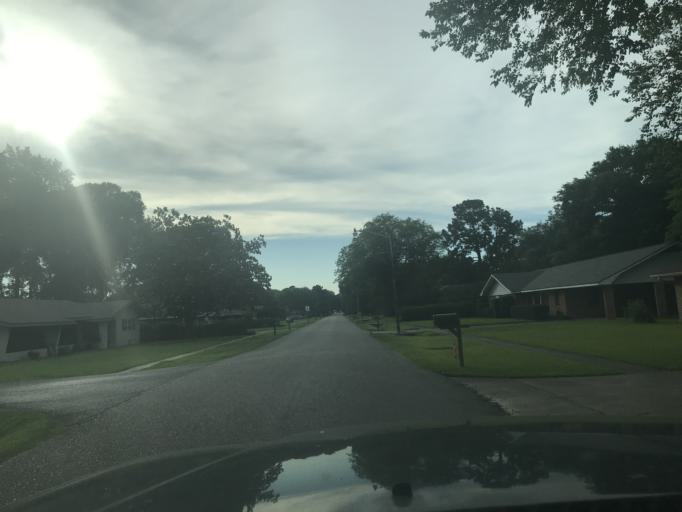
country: US
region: Louisiana
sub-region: Lafayette Parish
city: Lafayette
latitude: 30.1931
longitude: -92.0499
